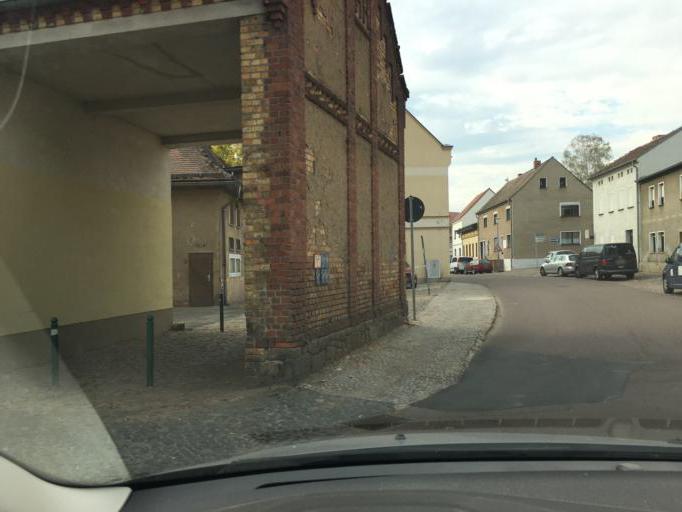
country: DE
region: Saxony-Anhalt
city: Landsberg
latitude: 51.5244
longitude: 12.1619
